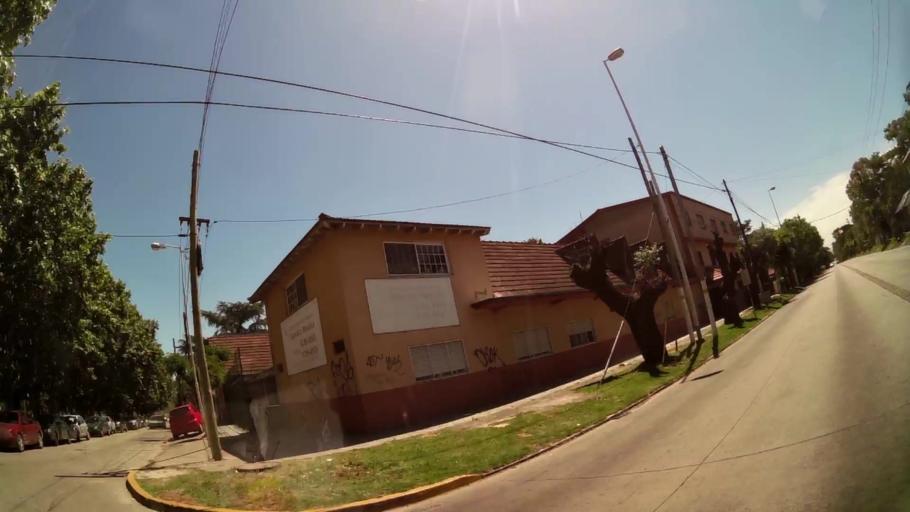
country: AR
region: Buenos Aires
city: Hurlingham
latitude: -34.5013
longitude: -58.6466
